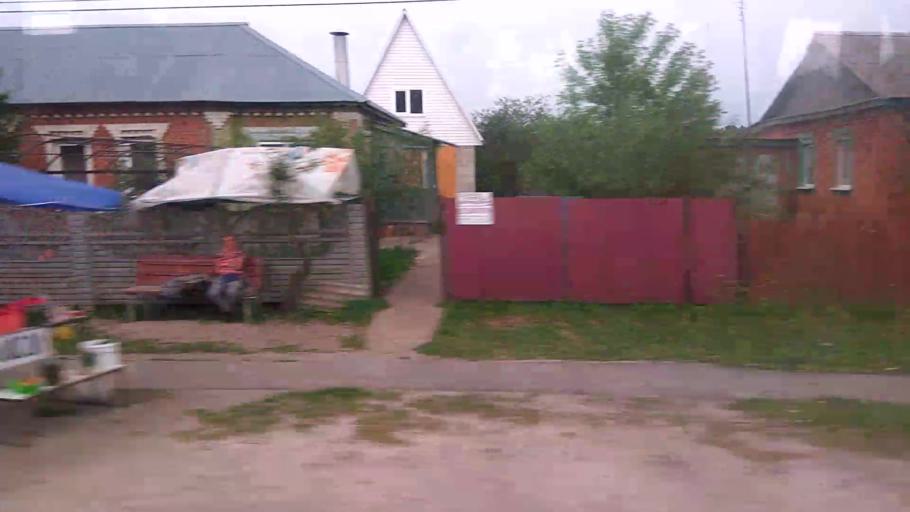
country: RU
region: Moskovskaya
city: Lukhovitsy
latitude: 54.9310
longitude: 39.0034
